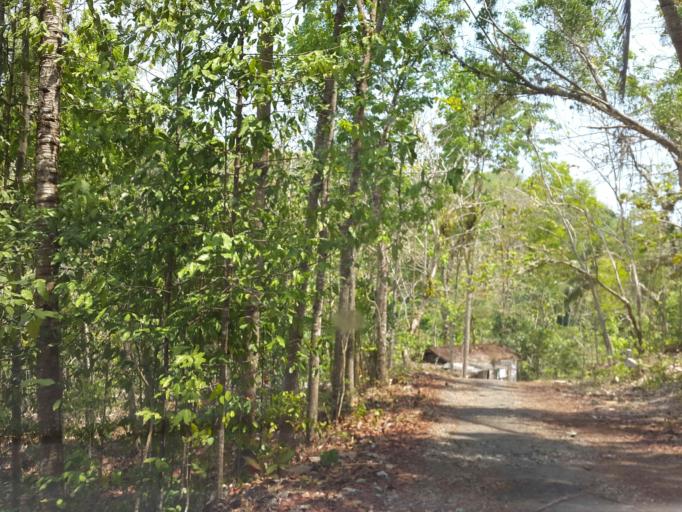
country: ID
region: East Java
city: Sudimoro
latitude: -8.2510
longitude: 111.2128
